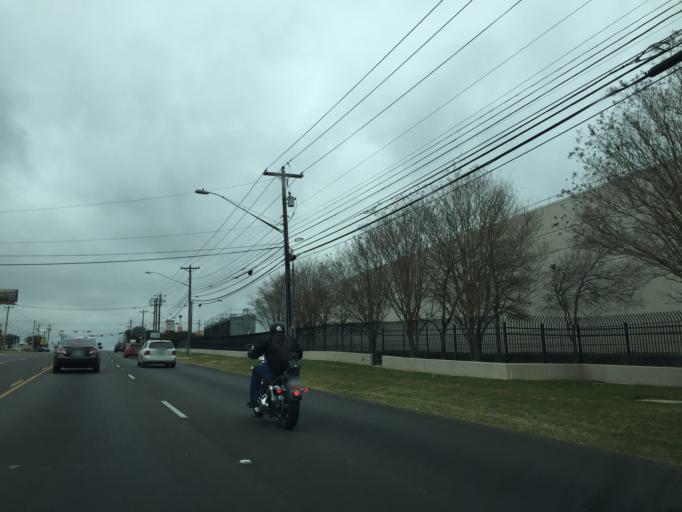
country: US
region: Texas
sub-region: Travis County
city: Wells Branch
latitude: 30.3838
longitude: -97.6854
